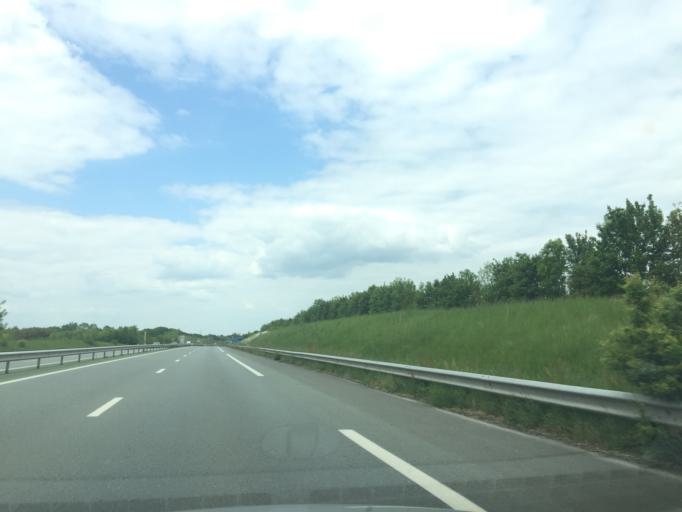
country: FR
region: Poitou-Charentes
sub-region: Departement des Deux-Sevres
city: Chauray
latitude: 46.3625
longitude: -0.3464
